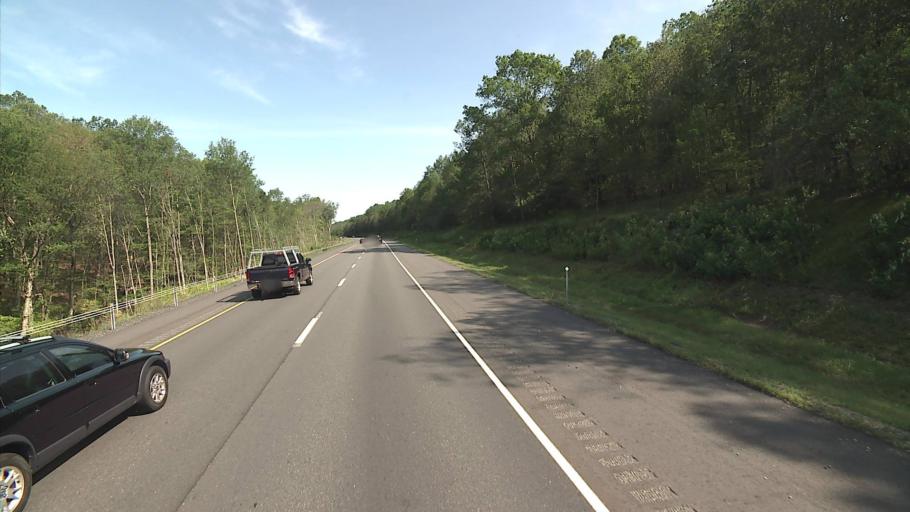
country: US
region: Connecticut
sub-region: Hartford County
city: Terramuggus
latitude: 41.6149
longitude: -72.4345
